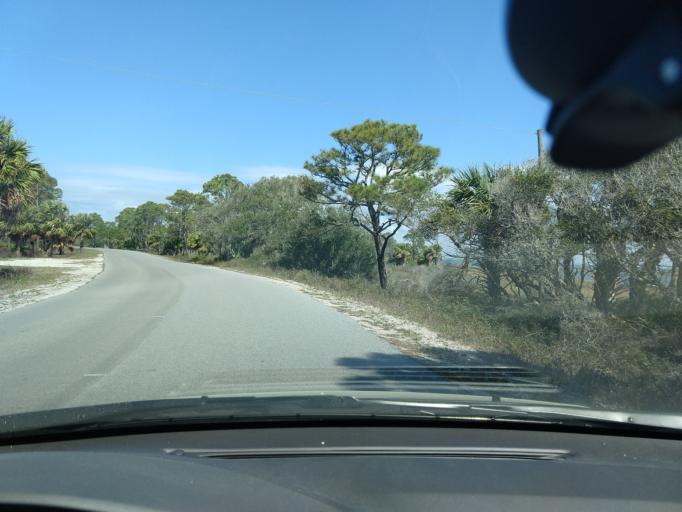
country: US
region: Florida
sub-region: Gulf County
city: Port Saint Joe
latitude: 29.7745
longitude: -85.4046
